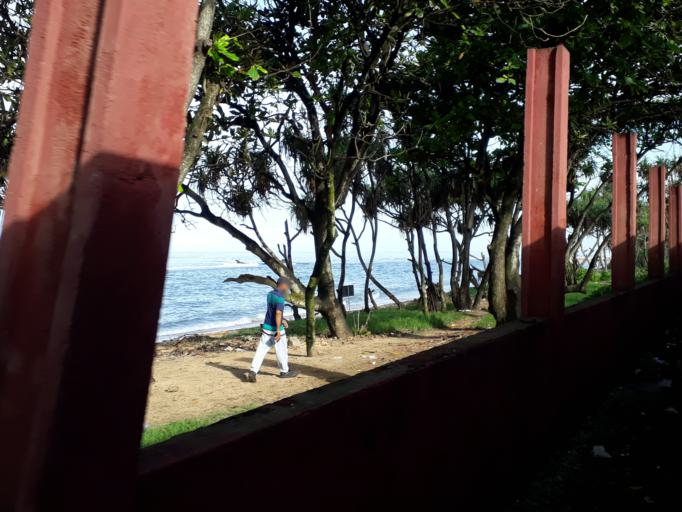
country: LK
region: Western
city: Galkissa
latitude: 6.8749
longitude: 79.8575
